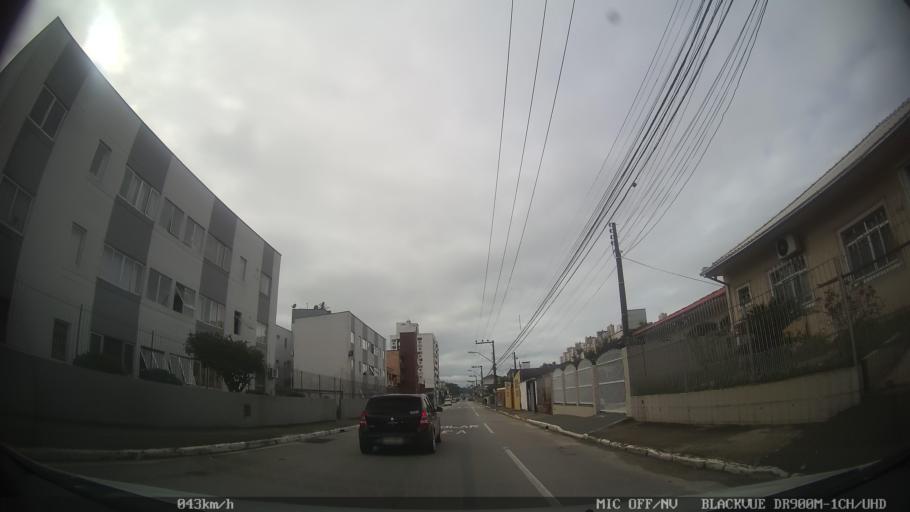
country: BR
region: Santa Catarina
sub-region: Sao Jose
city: Campinas
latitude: -27.5581
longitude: -48.6282
